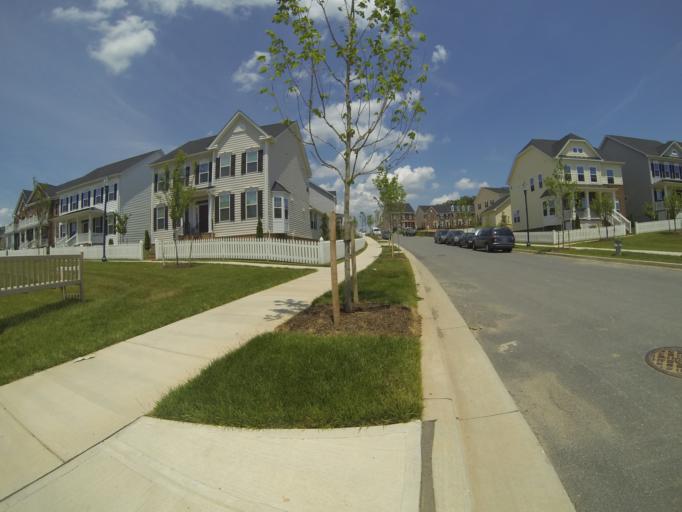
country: US
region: Maryland
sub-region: Montgomery County
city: Clarksburg
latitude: 39.2264
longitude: -77.2403
